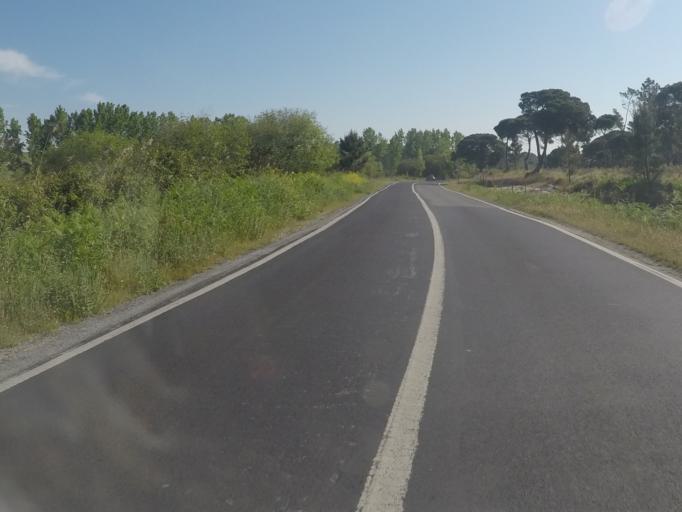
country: PT
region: Setubal
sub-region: Sesimbra
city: Sesimbra
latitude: 38.5302
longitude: -9.1268
